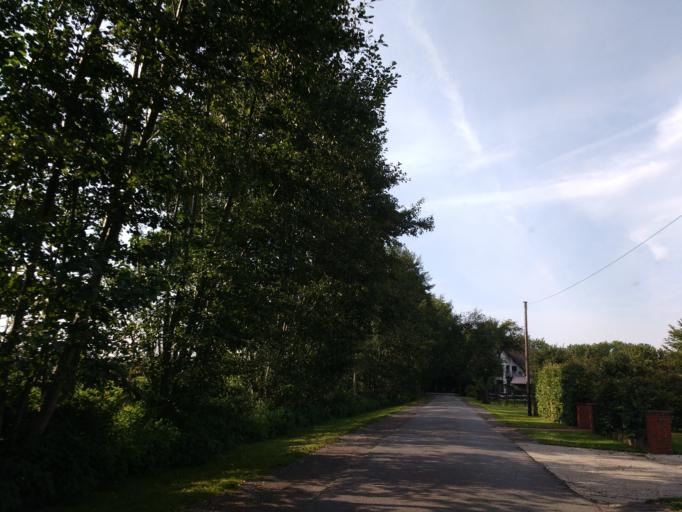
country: DE
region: North Rhine-Westphalia
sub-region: Regierungsbezirk Detmold
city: Delbruck
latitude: 51.7694
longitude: 8.5961
